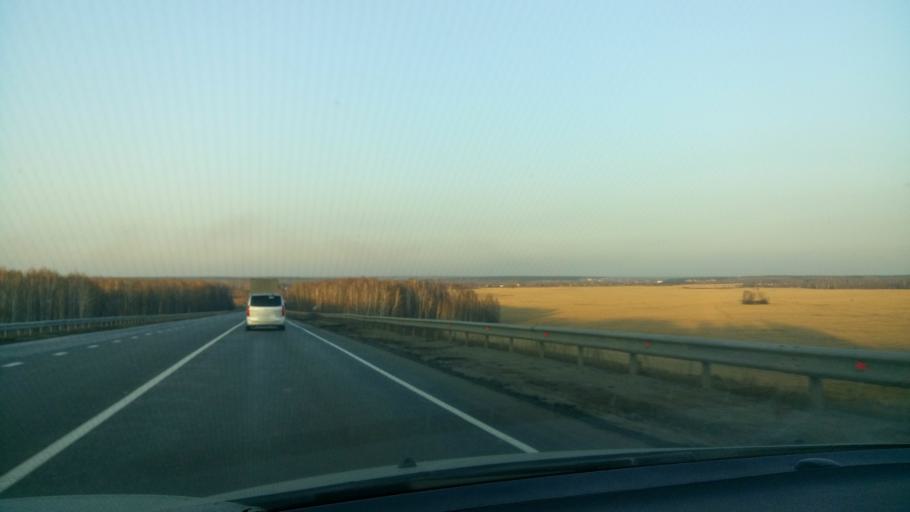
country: RU
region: Sverdlovsk
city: Yelanskiy
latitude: 56.7942
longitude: 62.5125
